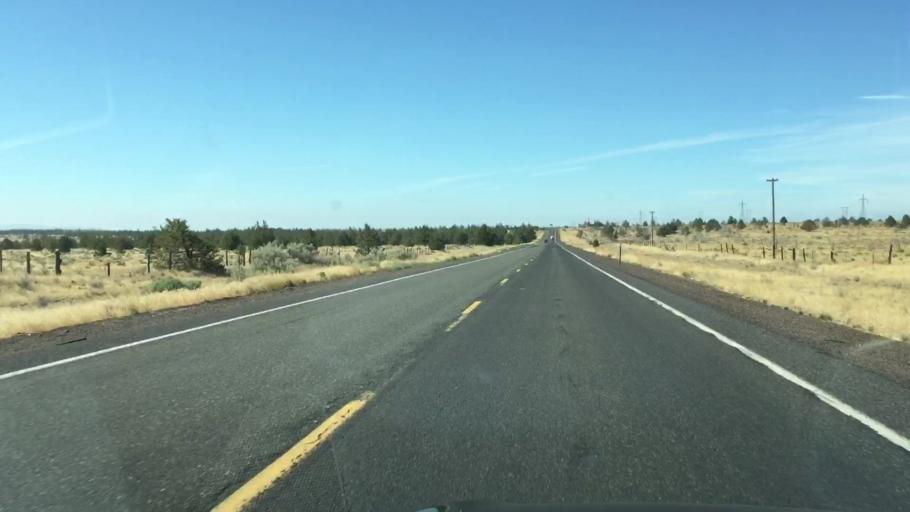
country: US
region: Oregon
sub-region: Jefferson County
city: Madras
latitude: 44.9327
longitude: -120.9342
